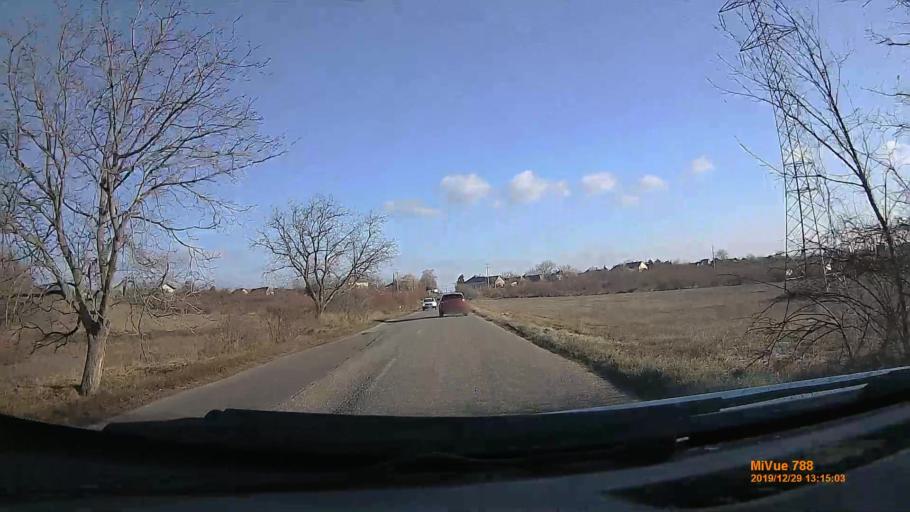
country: HU
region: Heves
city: Domoszlo
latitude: 47.8285
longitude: 20.1055
